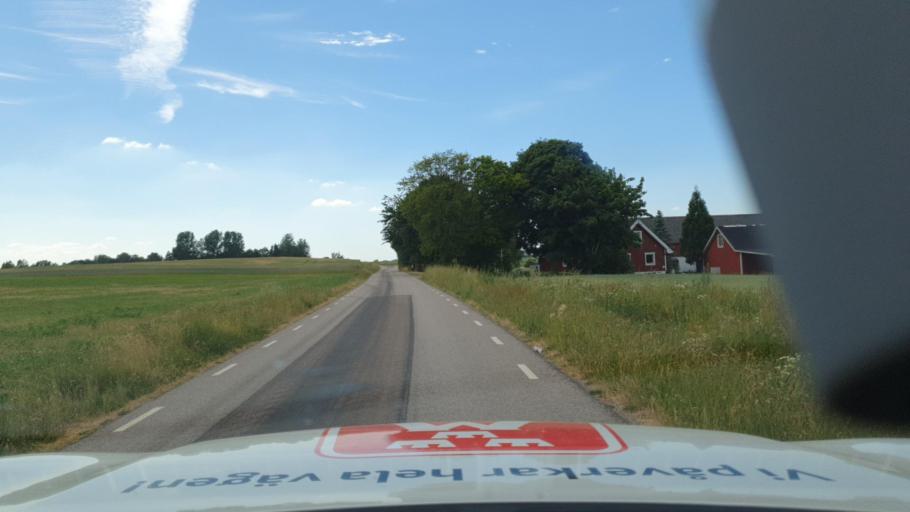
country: SE
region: Skane
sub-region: Sjobo Kommun
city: Sjoebo
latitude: 55.6337
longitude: 13.8230
